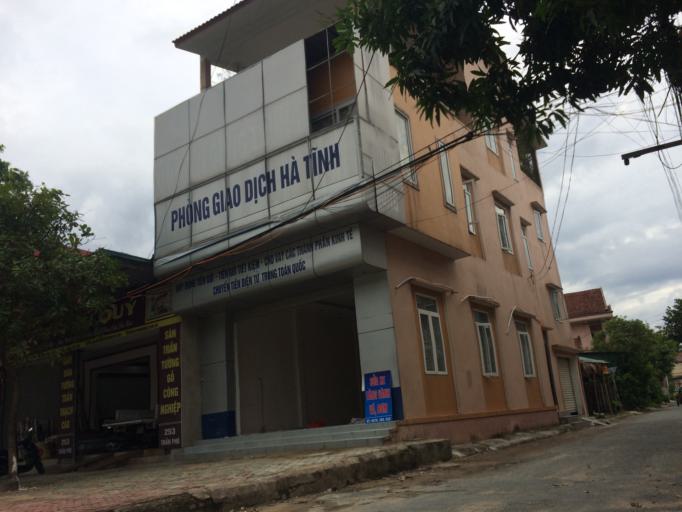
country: VN
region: Ha Tinh
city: Ha Tinh
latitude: 18.3466
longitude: 105.8876
